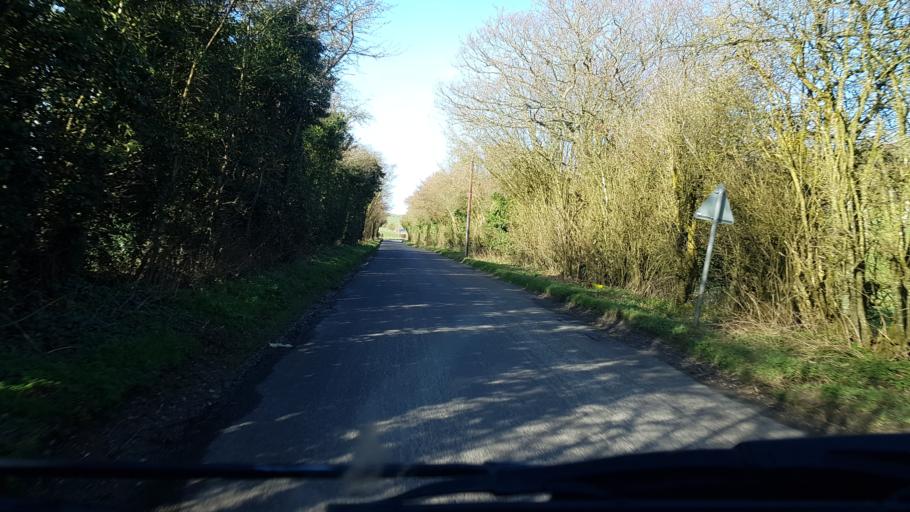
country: GB
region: England
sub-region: Wiltshire
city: Huish
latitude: 51.3894
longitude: -1.8170
